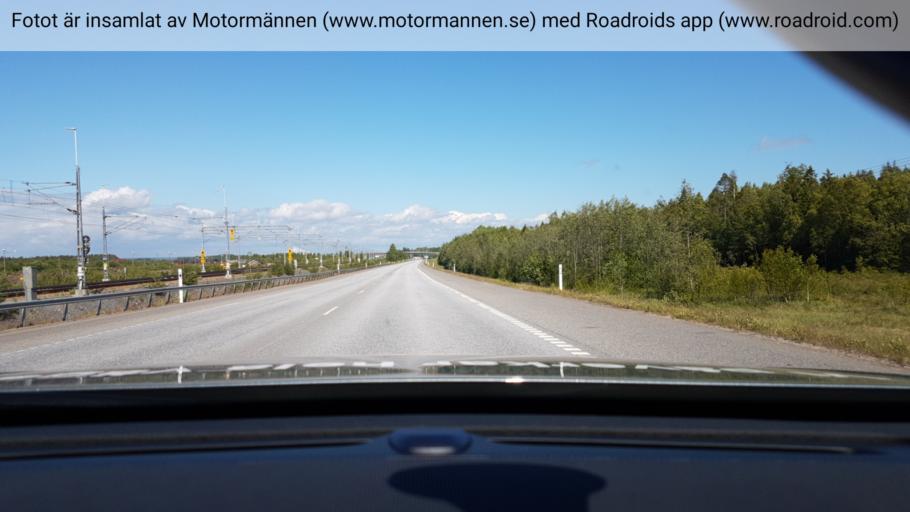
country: SE
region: Vaesterbotten
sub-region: Umea Kommun
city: Umea
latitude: 63.7835
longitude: 20.3204
